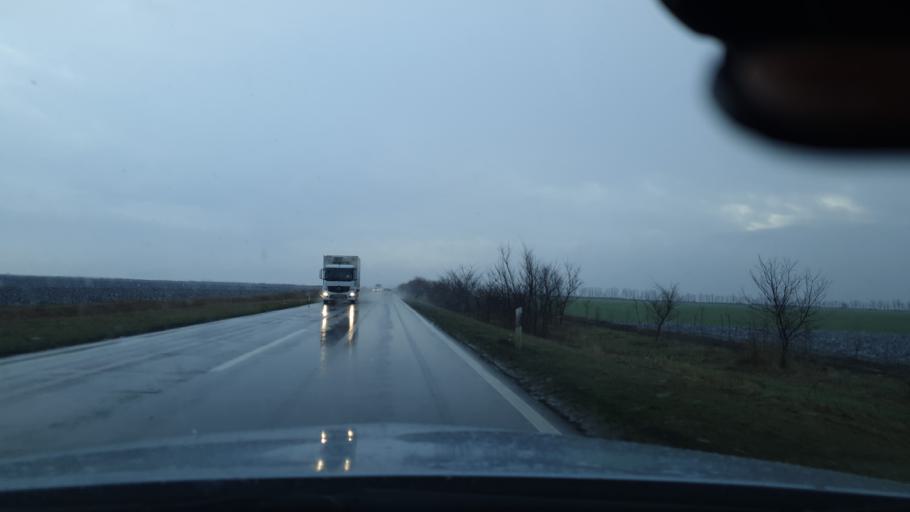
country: RS
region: Autonomna Pokrajina Vojvodina
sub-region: Juznobanatski Okrug
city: Pancevo
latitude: 44.8484
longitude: 20.7776
